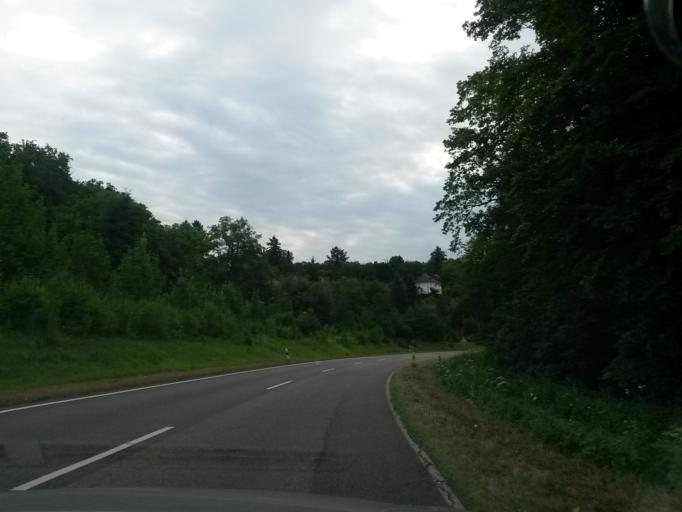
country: DE
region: Baden-Wuerttemberg
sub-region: Karlsruhe Region
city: Ispringen
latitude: 48.8966
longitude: 8.6544
